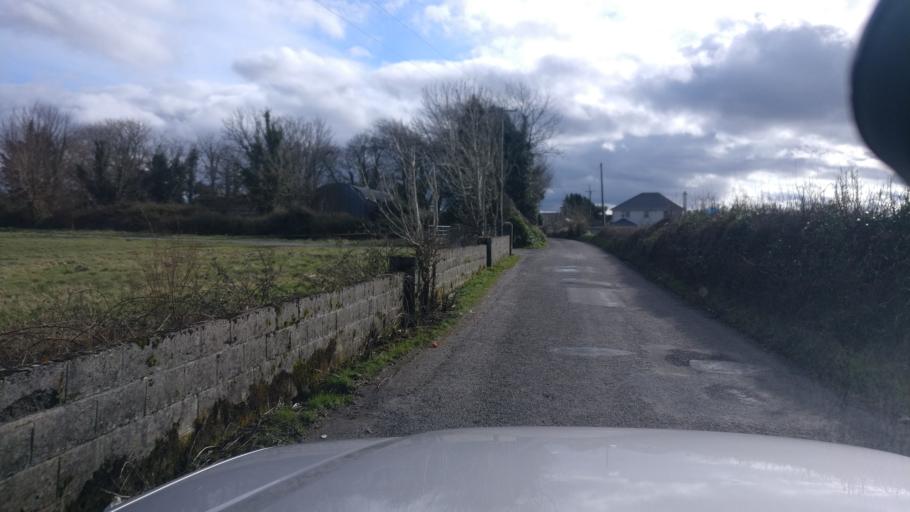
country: IE
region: Connaught
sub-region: County Galway
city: Loughrea
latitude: 53.1936
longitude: -8.5406
